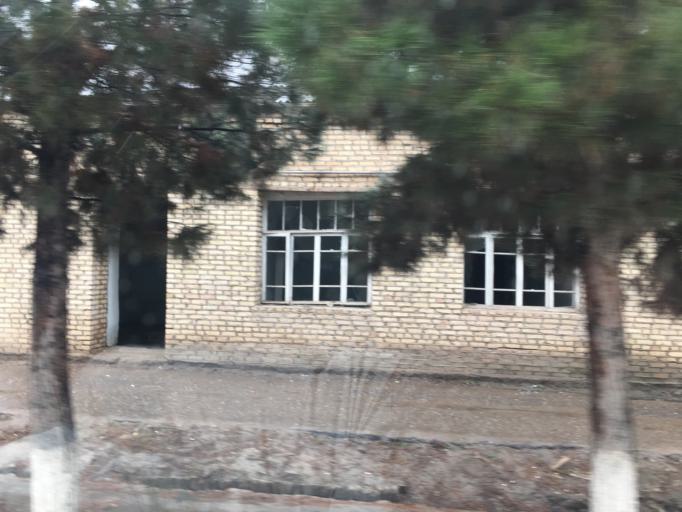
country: TM
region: Mary
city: Yoloeten
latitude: 37.2998
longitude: 62.3603
